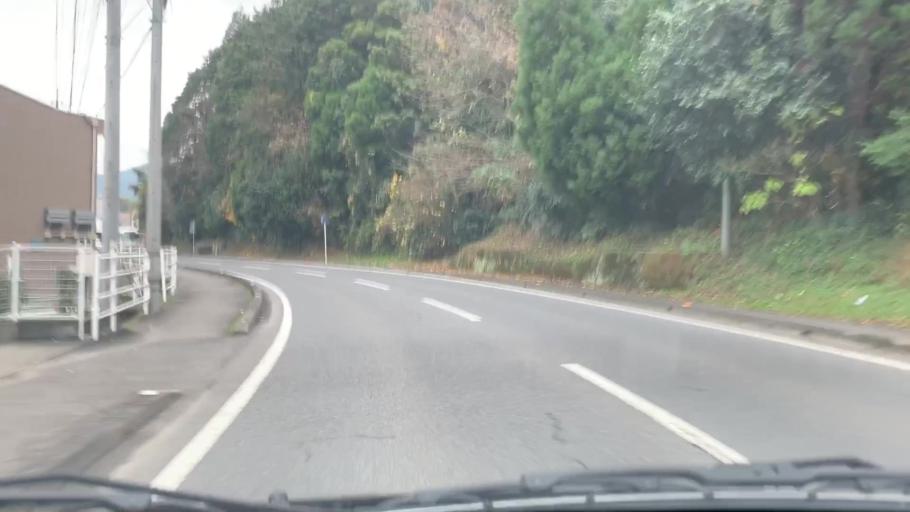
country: JP
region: Saga Prefecture
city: Takeocho-takeo
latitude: 33.1914
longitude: 130.0327
